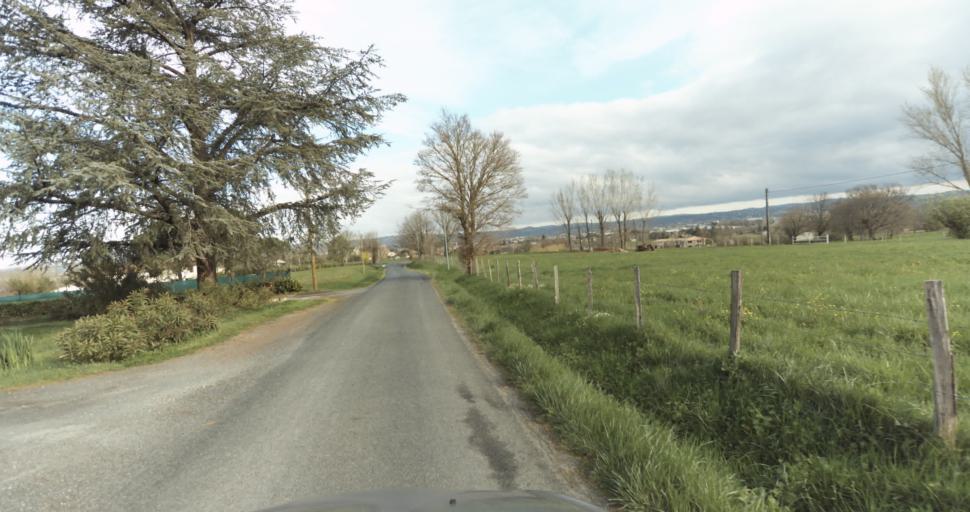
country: FR
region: Midi-Pyrenees
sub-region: Departement du Tarn
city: Puygouzon
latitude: 43.9071
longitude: 2.1748
